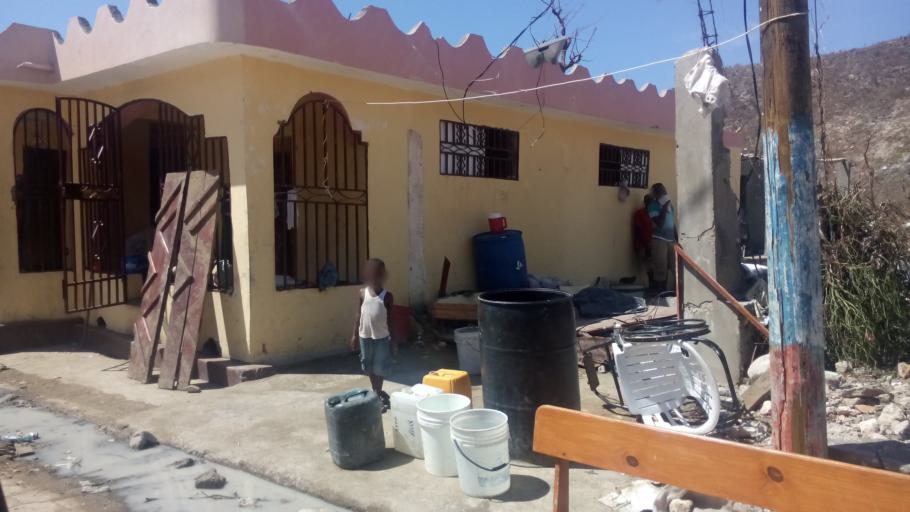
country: HT
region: Sud
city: Port-a-Piment
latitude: 18.2617
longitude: -74.0995
